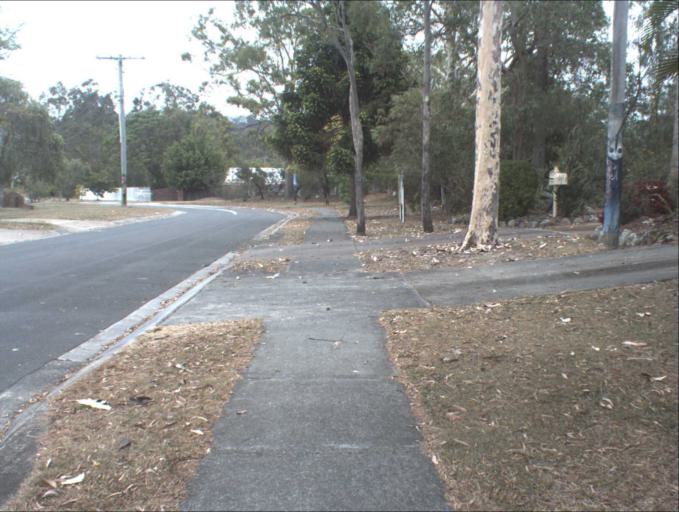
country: AU
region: Queensland
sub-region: Logan
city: Slacks Creek
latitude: -27.6656
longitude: 153.1805
